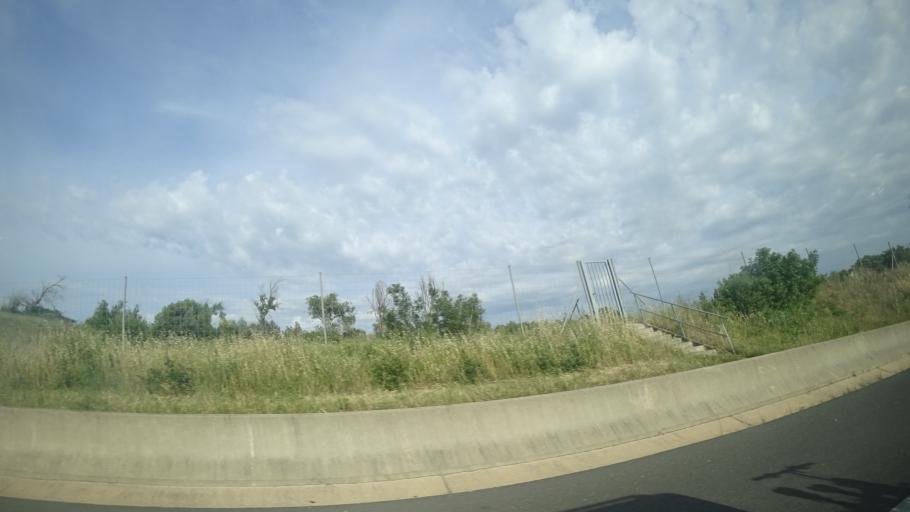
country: FR
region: Languedoc-Roussillon
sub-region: Departement de l'Herault
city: Nebian
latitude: 43.6472
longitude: 3.4498
